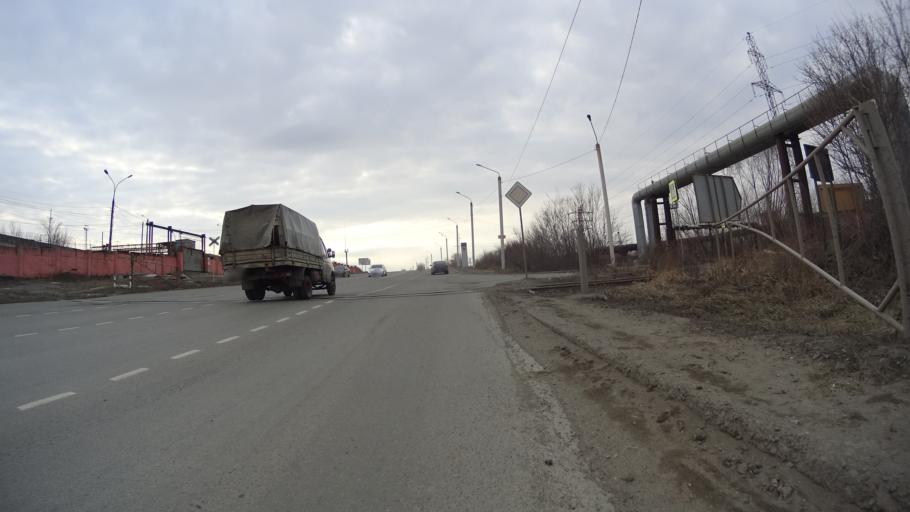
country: RU
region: Chelyabinsk
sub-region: Gorod Chelyabinsk
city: Chelyabinsk
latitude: 55.1579
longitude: 61.4876
